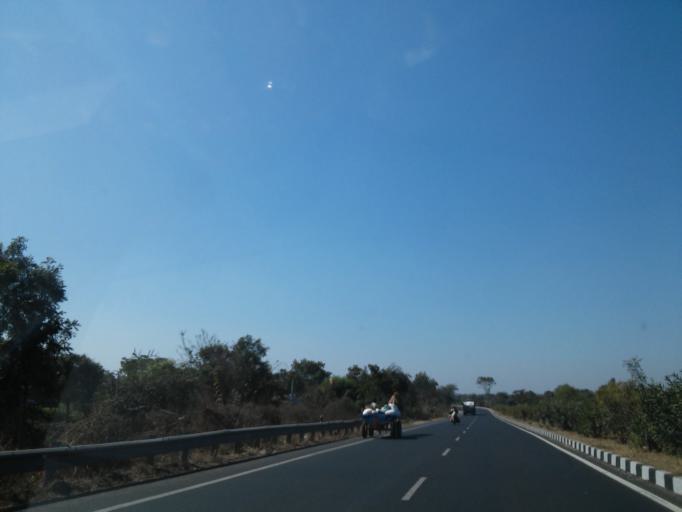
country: IN
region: Gujarat
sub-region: Sabar Kantha
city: Modasa
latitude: 23.6774
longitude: 73.3498
